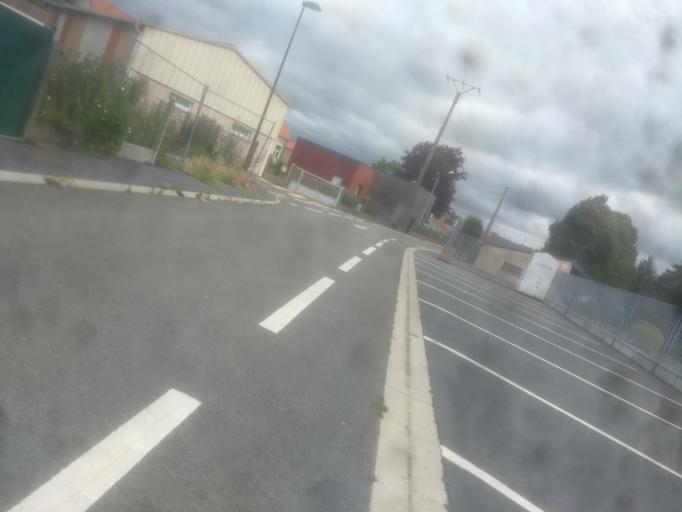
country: FR
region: Nord-Pas-de-Calais
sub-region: Departement du Pas-de-Calais
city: Thelus
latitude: 50.3540
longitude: 2.7985
